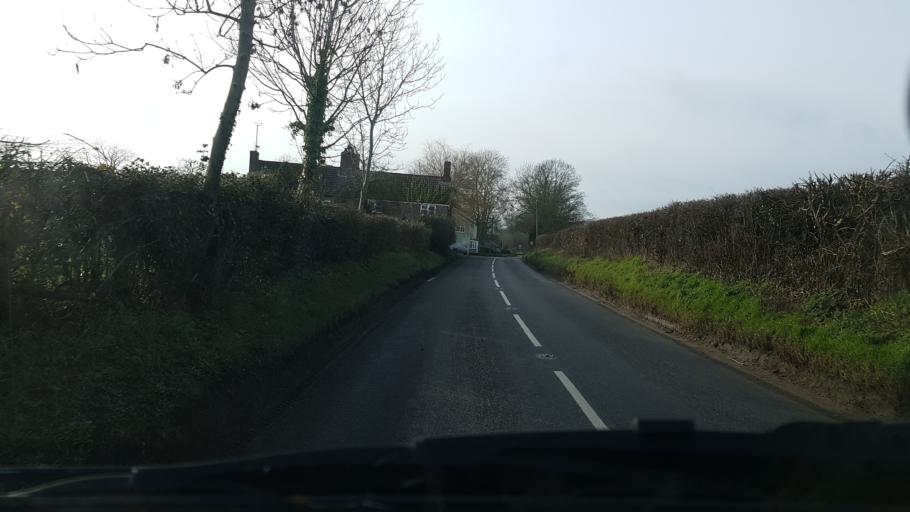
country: GB
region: England
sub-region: Wiltshire
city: Pewsey
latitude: 51.3468
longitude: -1.7381
